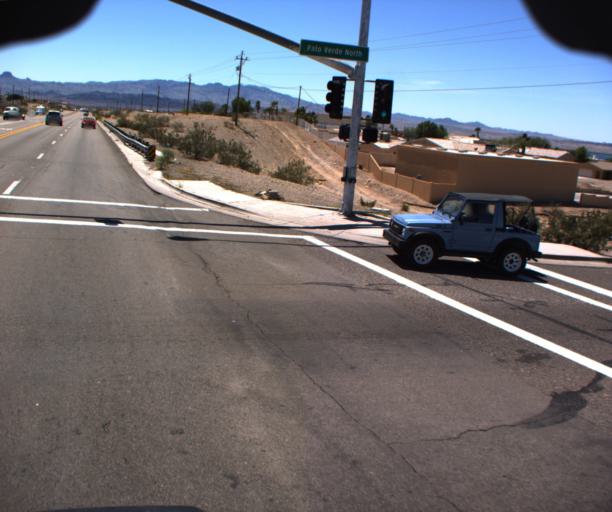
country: US
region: Arizona
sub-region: Mohave County
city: Lake Havasu City
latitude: 34.5172
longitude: -114.3496
